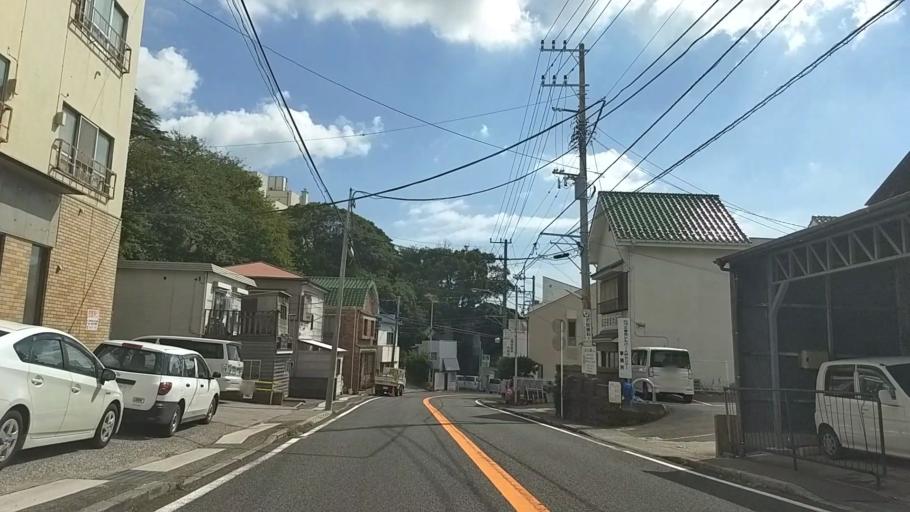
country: JP
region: Kanagawa
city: Miura
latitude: 35.1441
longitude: 139.6198
